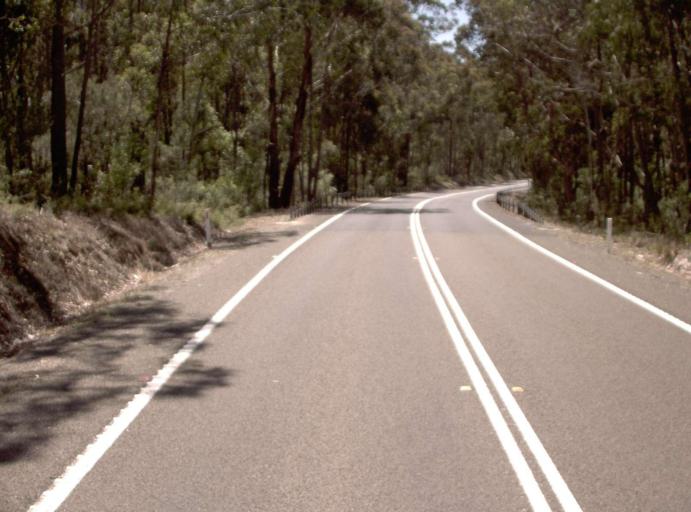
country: AU
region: Victoria
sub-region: East Gippsland
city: Lakes Entrance
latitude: -37.7584
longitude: 148.0615
